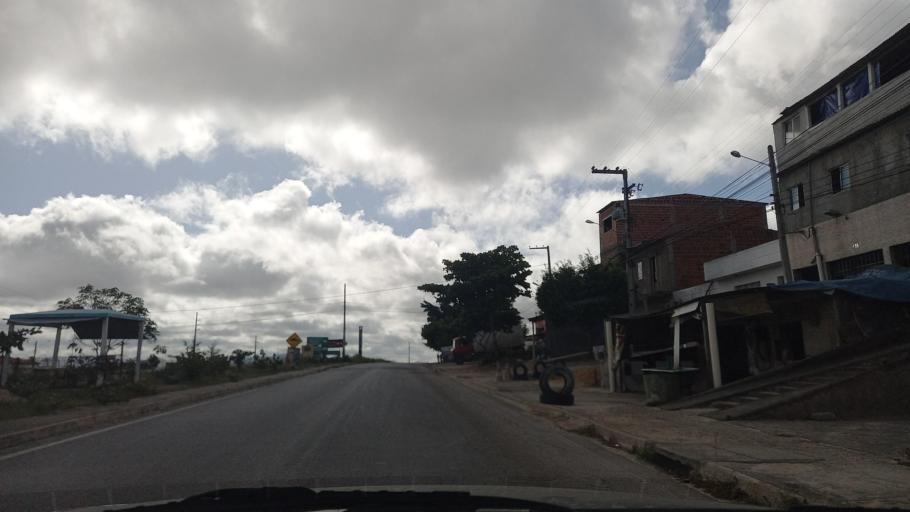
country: BR
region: Pernambuco
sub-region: Caruaru
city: Caruaru
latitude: -8.3089
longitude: -36.0245
